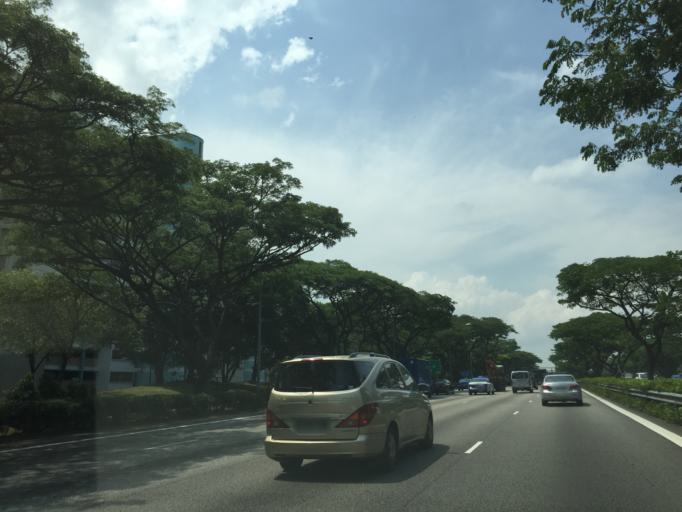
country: SG
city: Singapore
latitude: 1.3303
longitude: 103.9149
